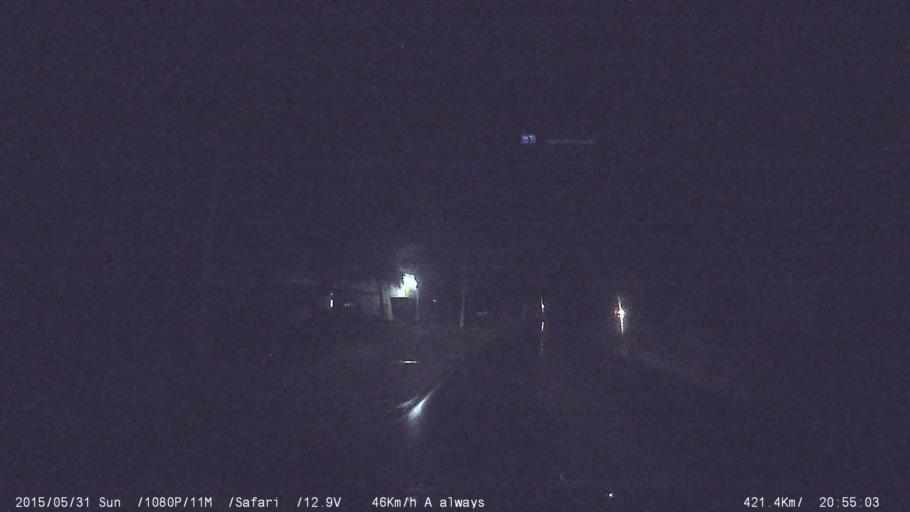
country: IN
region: Karnataka
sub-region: Ramanagara
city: Channapatna
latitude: 12.6128
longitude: 77.2159
